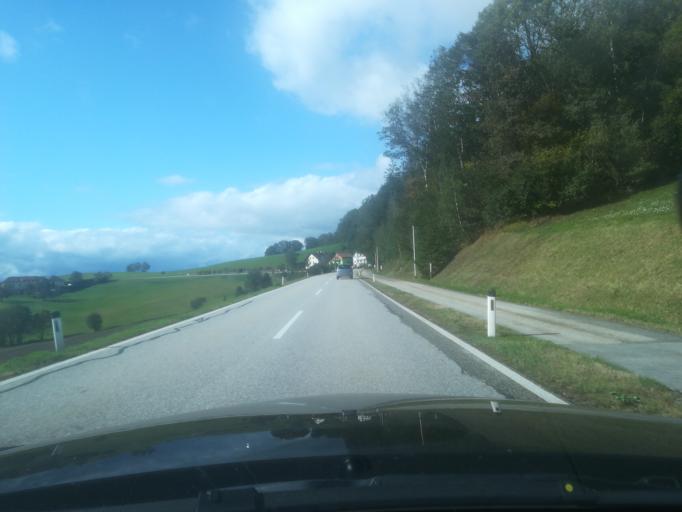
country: AT
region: Upper Austria
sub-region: Politischer Bezirk Urfahr-Umgebung
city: Eidenberg
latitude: 48.3619
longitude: 14.2515
